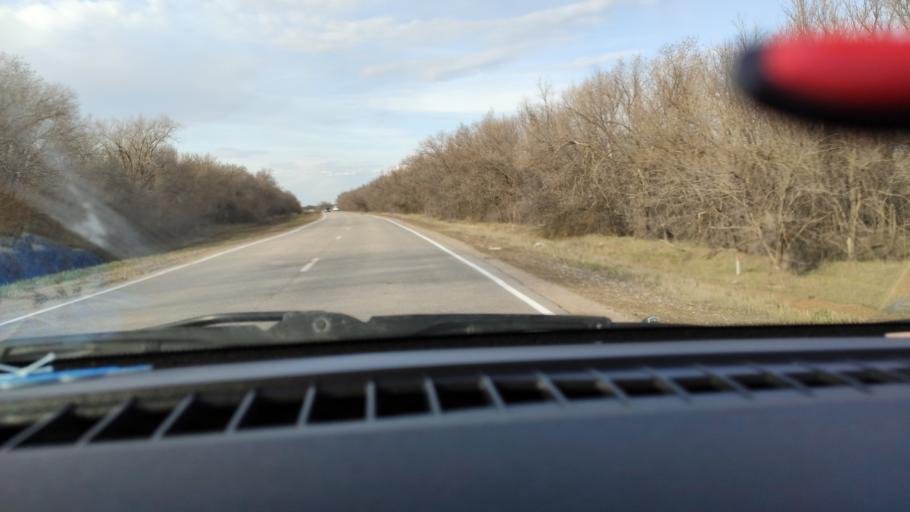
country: RU
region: Saratov
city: Privolzhskiy
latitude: 51.2489
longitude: 45.9375
